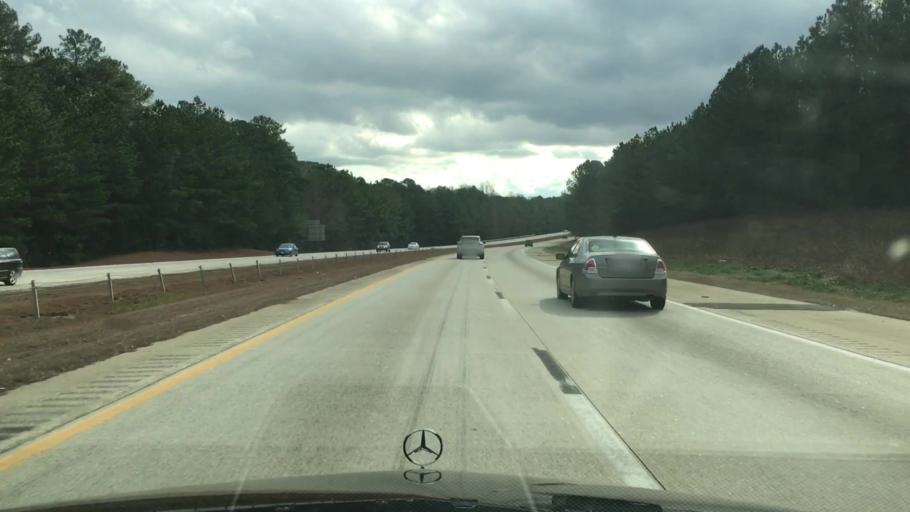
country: US
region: North Carolina
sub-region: Wake County
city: Garner
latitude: 35.6758
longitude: -78.5640
